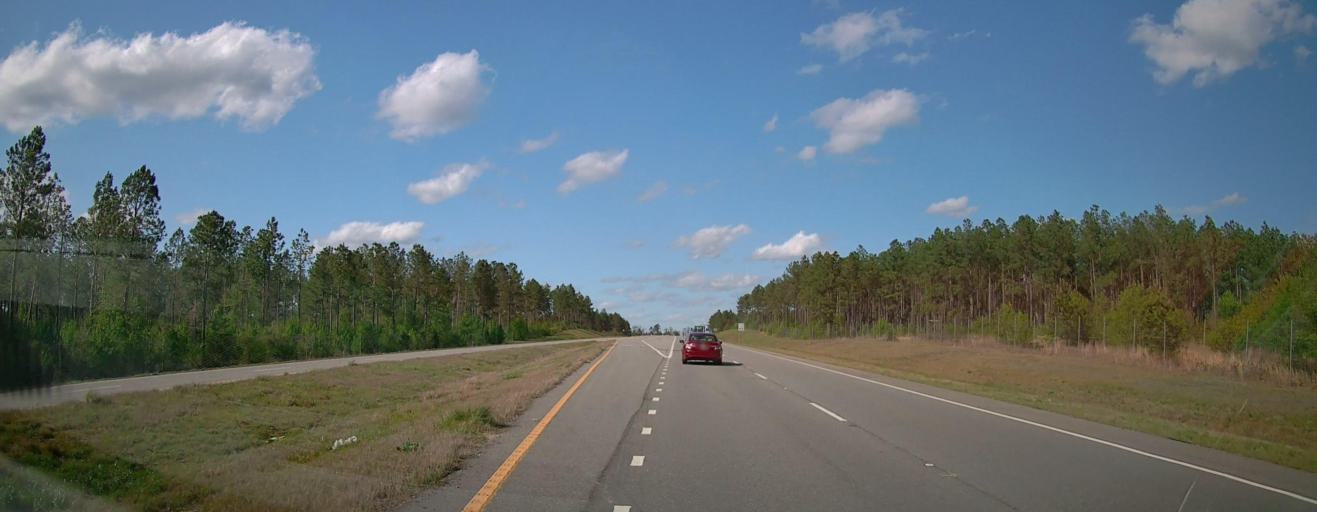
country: US
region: Georgia
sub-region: Baldwin County
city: Hardwick
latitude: 32.9877
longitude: -83.2056
